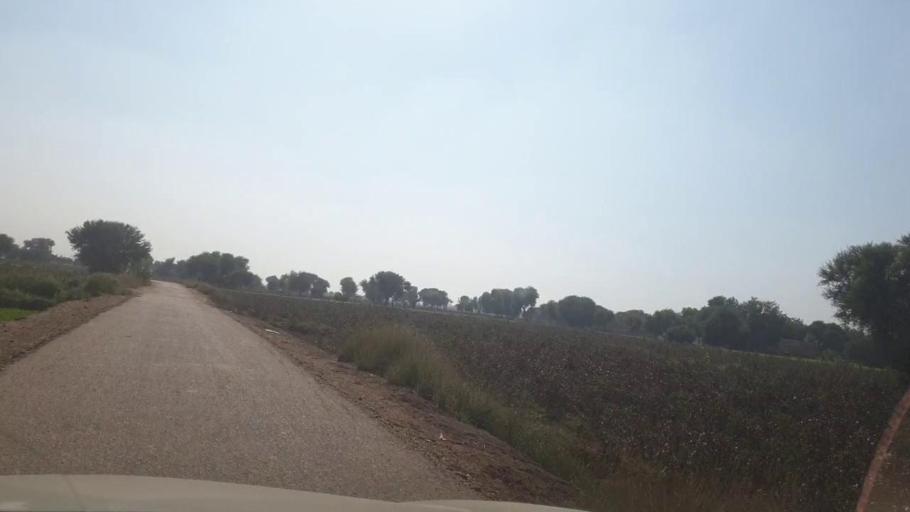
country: PK
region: Sindh
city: Bhan
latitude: 26.5799
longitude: 67.6903
